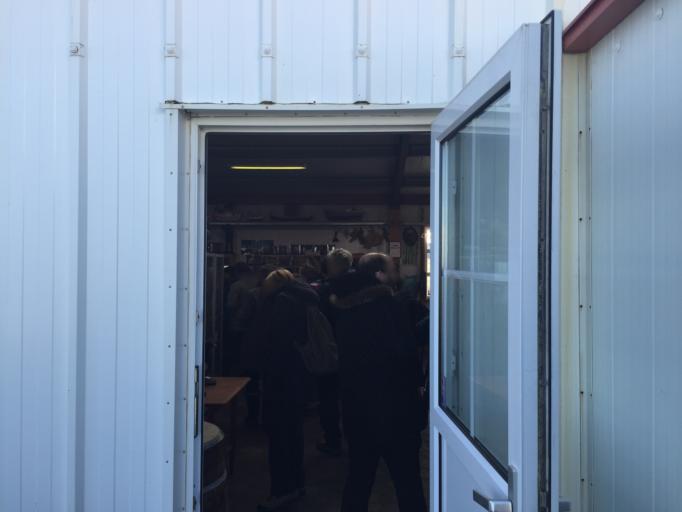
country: IS
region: West
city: Stykkisholmur
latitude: 64.9979
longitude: -22.9636
